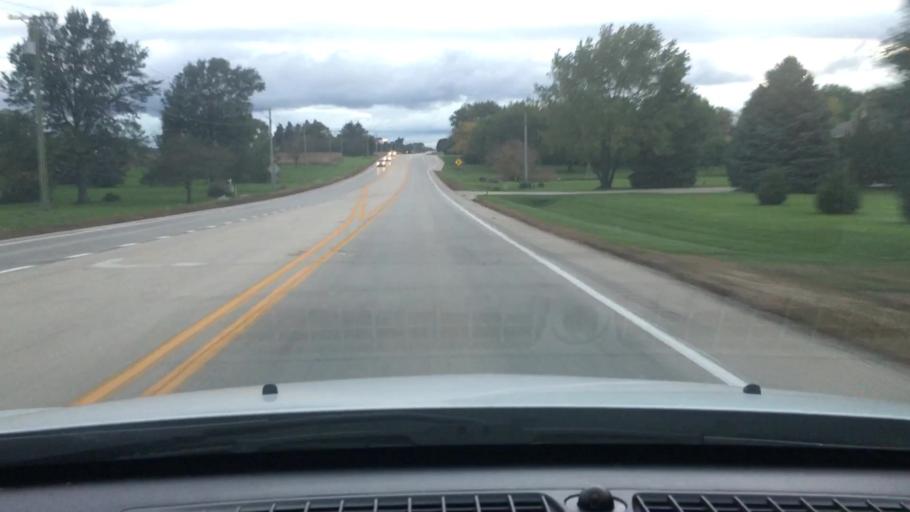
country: US
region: Illinois
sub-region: DeKalb County
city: Malta
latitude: 41.9362
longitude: -88.8238
